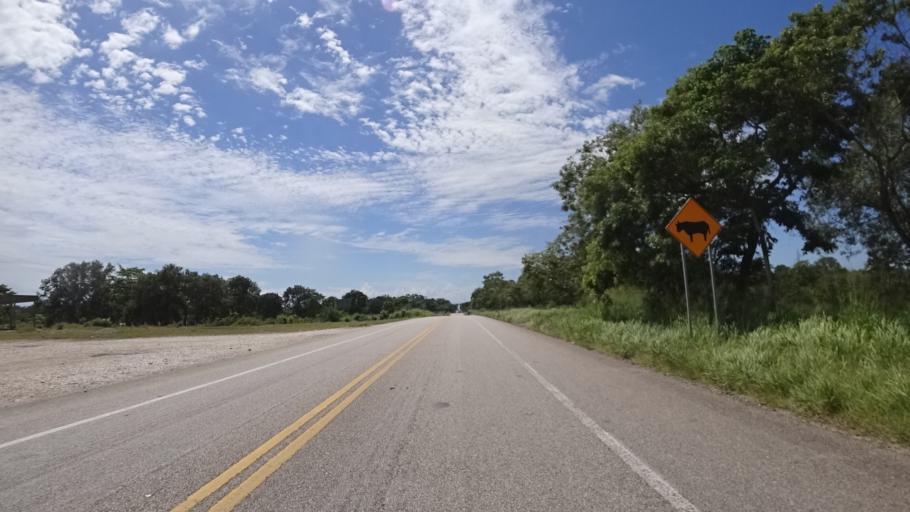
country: MX
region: Chiapas
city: Emiliano Zapata
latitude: 17.7588
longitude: -91.8727
